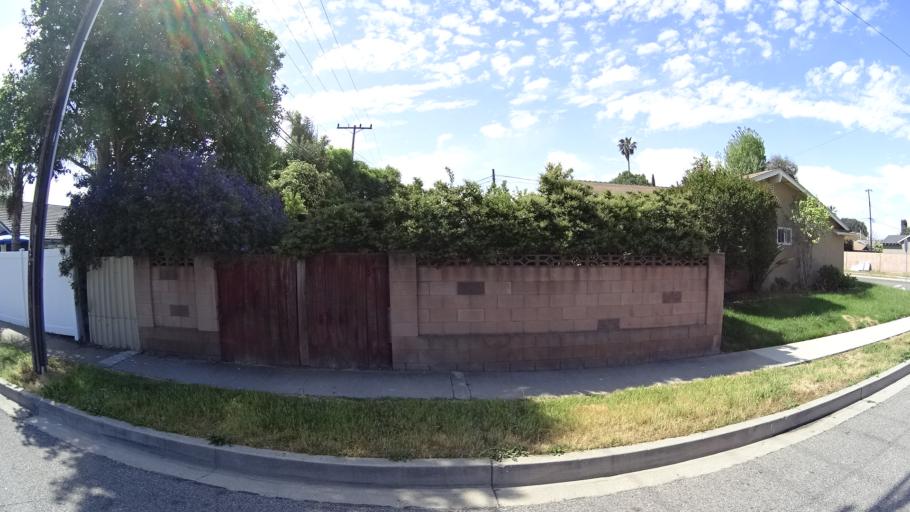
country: US
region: California
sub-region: Ventura County
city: Casa Conejo
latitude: 34.1832
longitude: -118.9388
